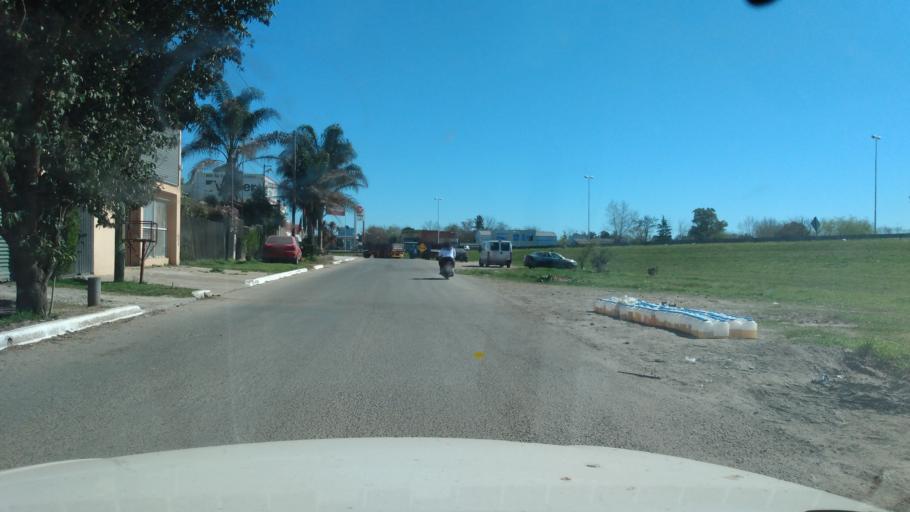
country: AR
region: Buenos Aires
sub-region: Partido de Lujan
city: Lujan
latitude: -34.5621
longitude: -59.0896
